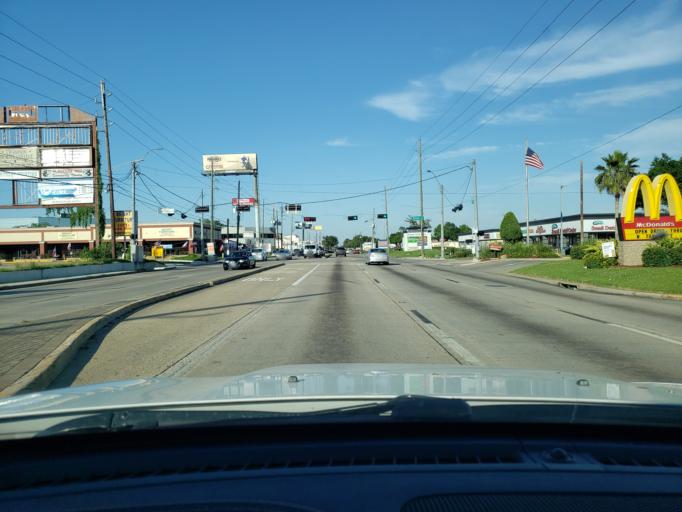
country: US
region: Texas
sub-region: Harris County
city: Hudson
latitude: 29.9852
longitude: -95.5031
